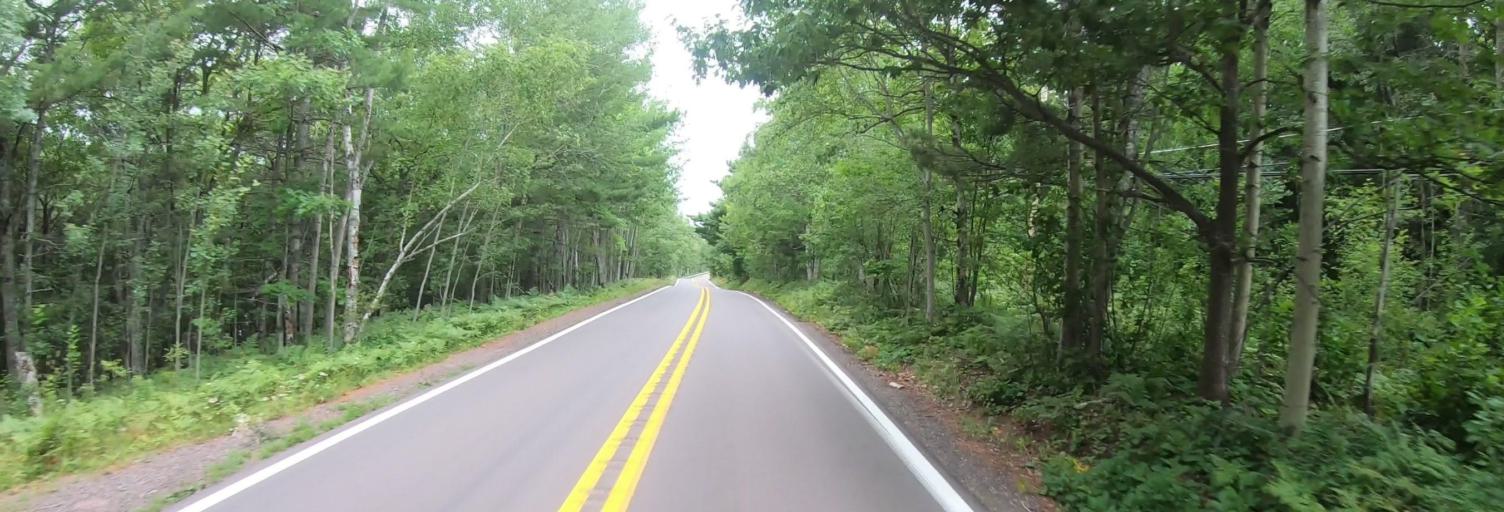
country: US
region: Michigan
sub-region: Keweenaw County
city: Eagle River
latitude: 47.4607
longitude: -88.1001
